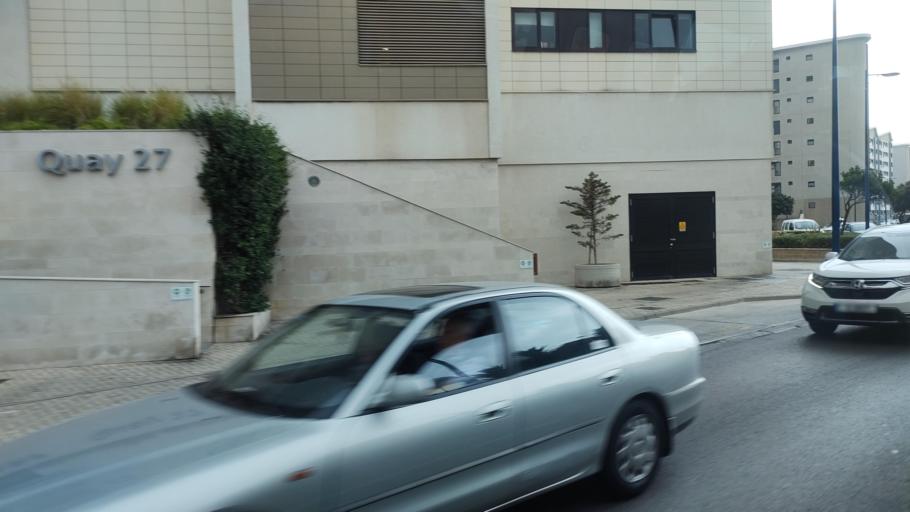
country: GI
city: Gibraltar
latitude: 36.1386
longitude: -5.3557
